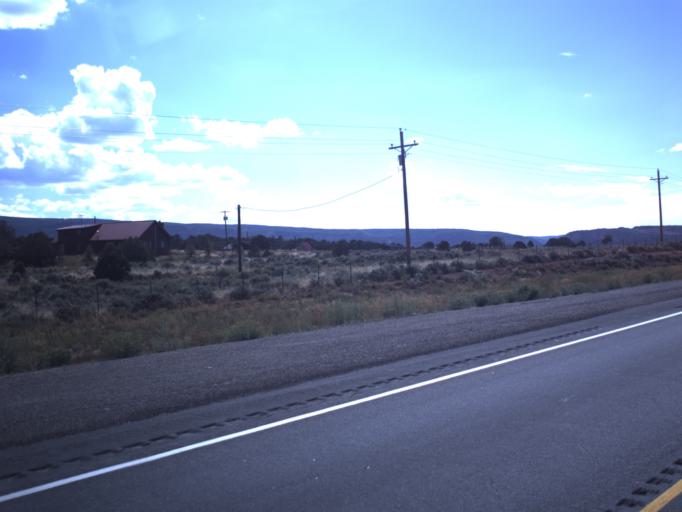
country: US
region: Utah
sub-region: Duchesne County
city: Duchesne
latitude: 40.2088
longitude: -110.8238
